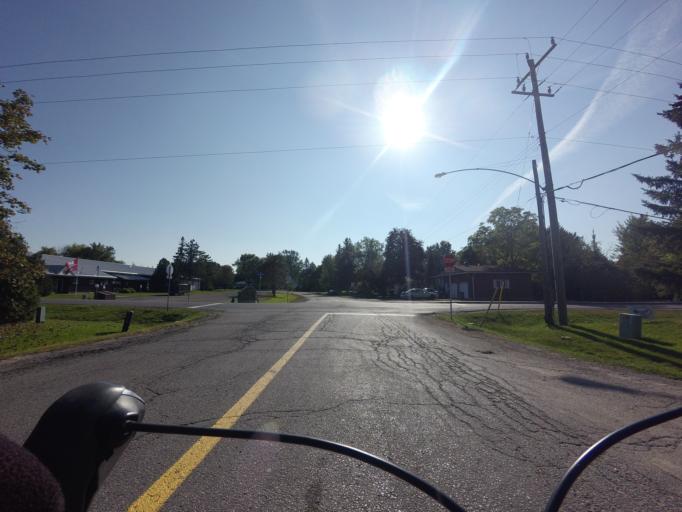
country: CA
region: Ontario
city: Bells Corners
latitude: 45.2291
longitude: -75.6793
